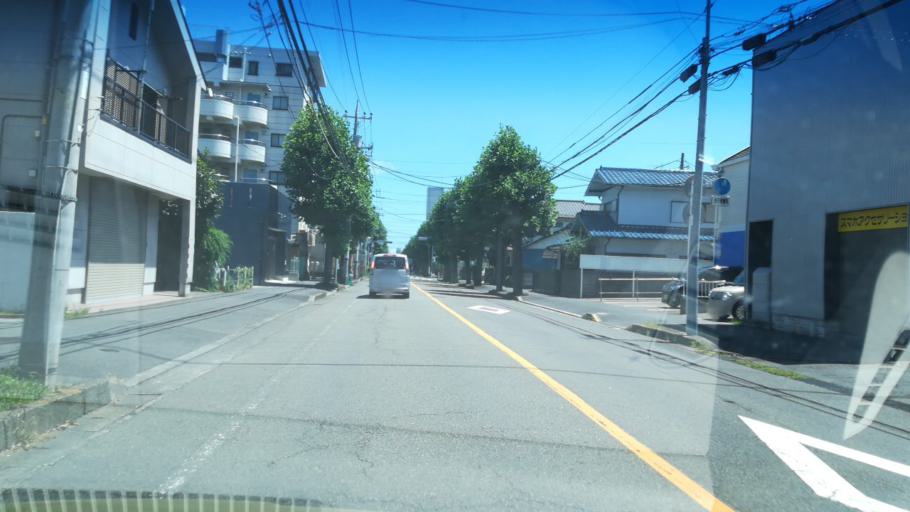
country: JP
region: Tokyo
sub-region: Machida-shi
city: Machida
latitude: 35.5752
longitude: 139.3801
